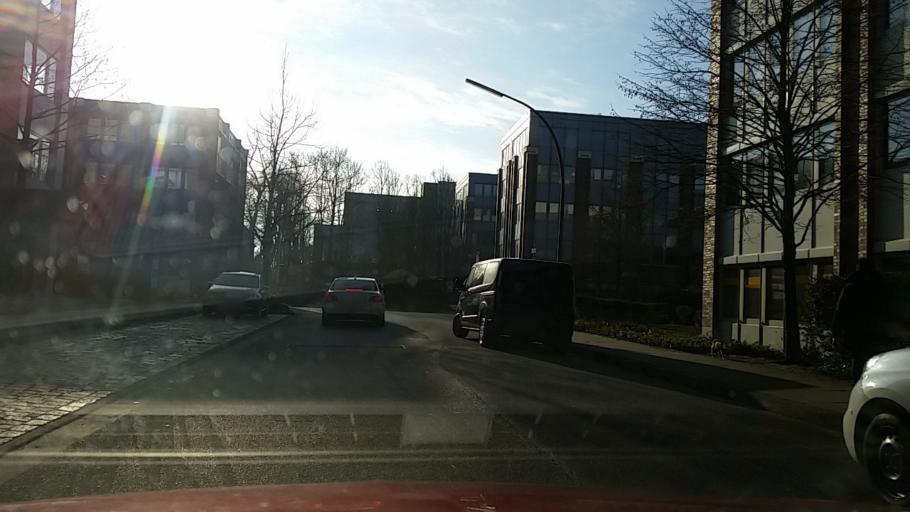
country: DE
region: Hamburg
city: Eidelstedt
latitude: 53.5750
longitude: 9.8885
